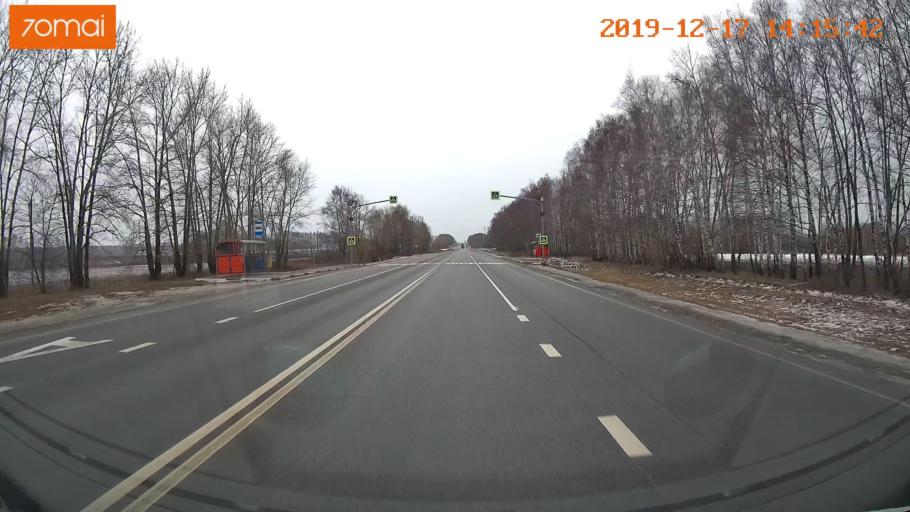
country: RU
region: Rjazan
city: Zakharovo
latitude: 54.4879
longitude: 39.4724
